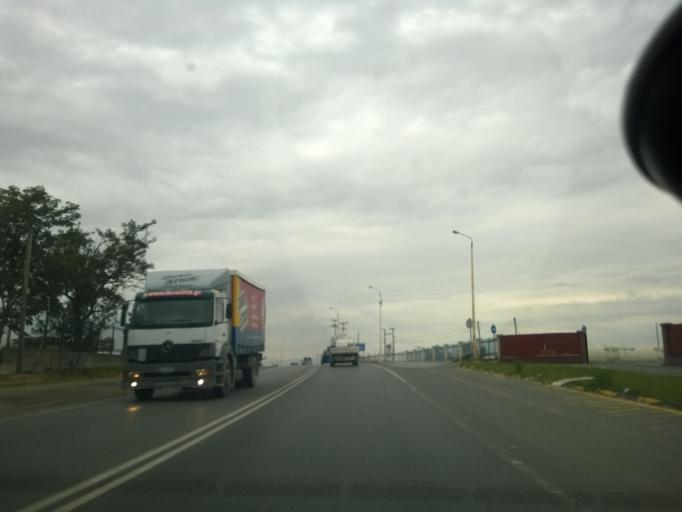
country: GR
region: Central Macedonia
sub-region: Nomos Pellis
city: Giannitsa
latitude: 40.7834
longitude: 22.3929
